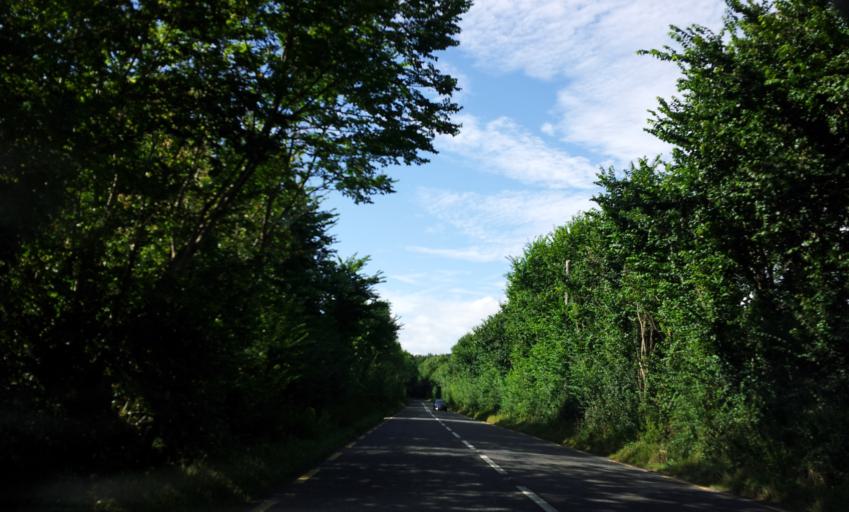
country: IE
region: Munster
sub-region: County Cork
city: Macroom
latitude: 51.9131
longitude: -9.0524
